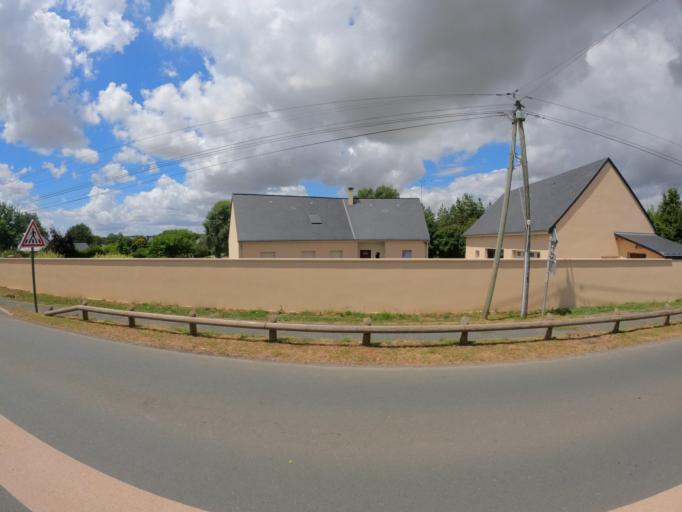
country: FR
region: Pays de la Loire
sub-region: Departement de Maine-et-Loire
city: Mire
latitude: 47.7613
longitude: -0.4869
